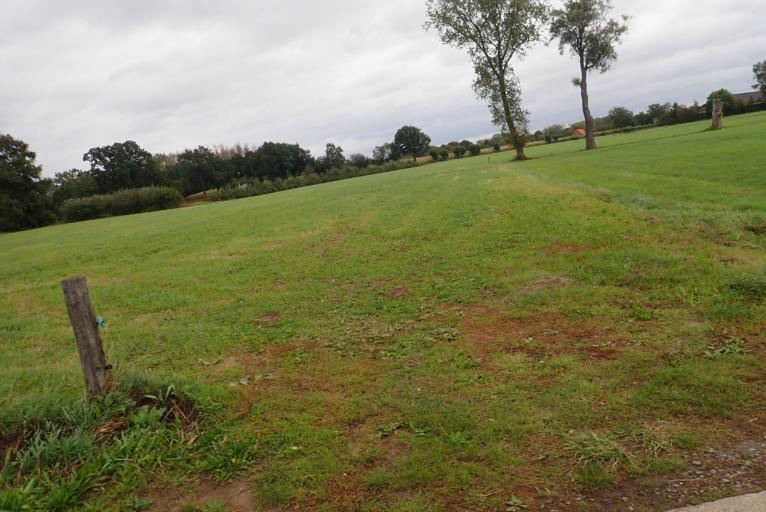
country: BE
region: Flanders
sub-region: Provincie Antwerpen
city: Heist-op-den-Berg
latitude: 51.0601
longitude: 4.7546
